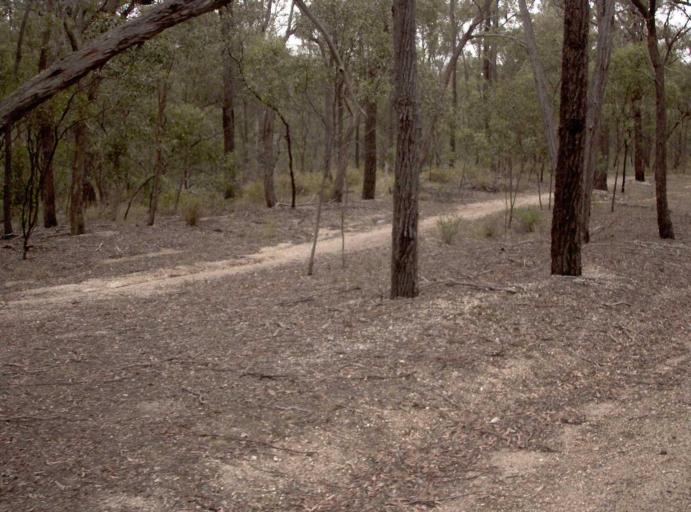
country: AU
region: Victoria
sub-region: Wellington
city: Heyfield
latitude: -37.9506
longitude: 146.7682
